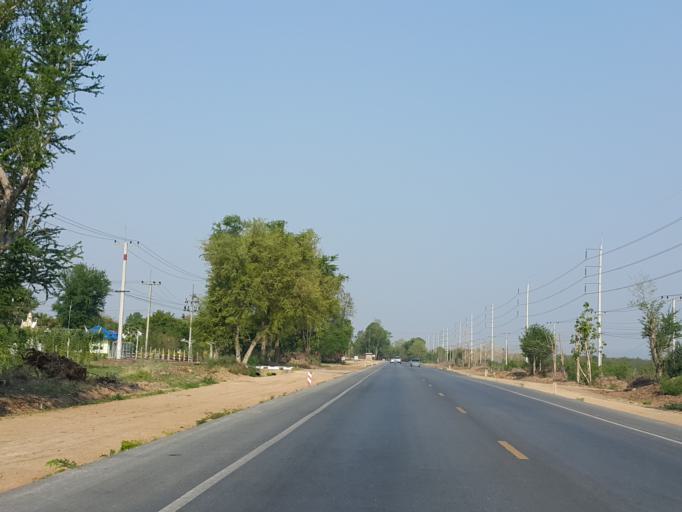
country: TH
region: Kanchanaburi
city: Sai Yok
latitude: 14.0892
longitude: 99.3198
